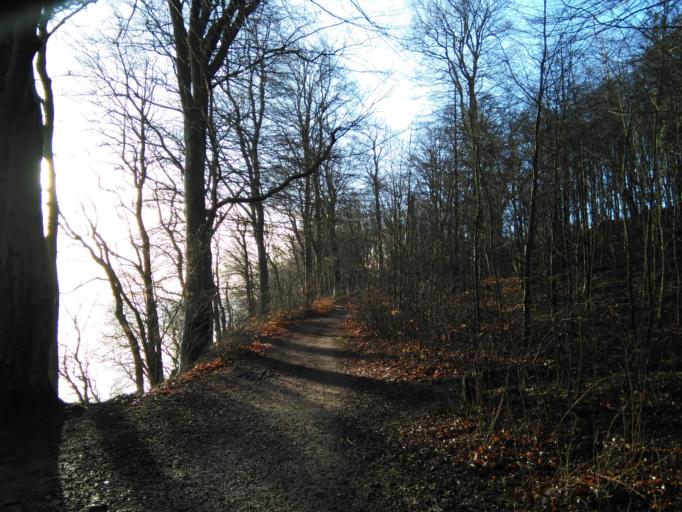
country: DK
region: Central Jutland
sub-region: Arhus Kommune
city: Arhus
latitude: 56.1157
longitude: 10.2283
